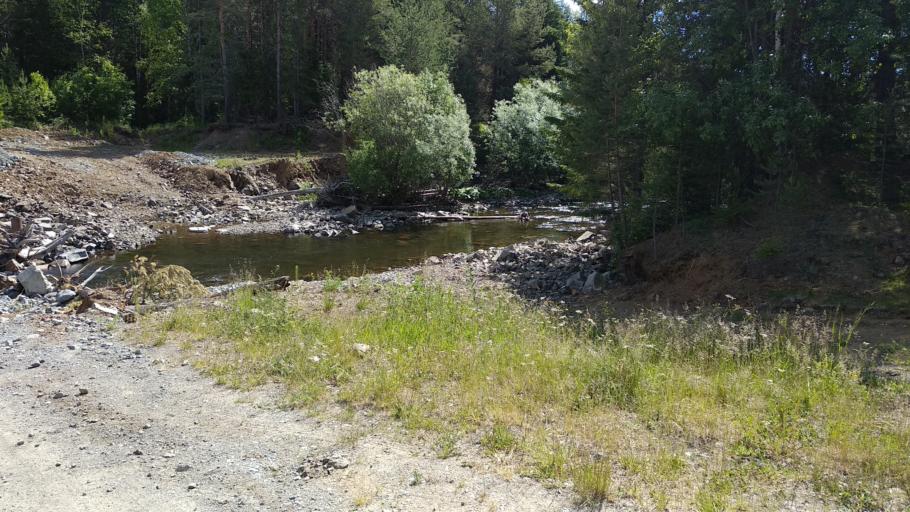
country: RU
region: Sverdlovsk
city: Severoural'sk
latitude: 60.1278
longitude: 59.8073
